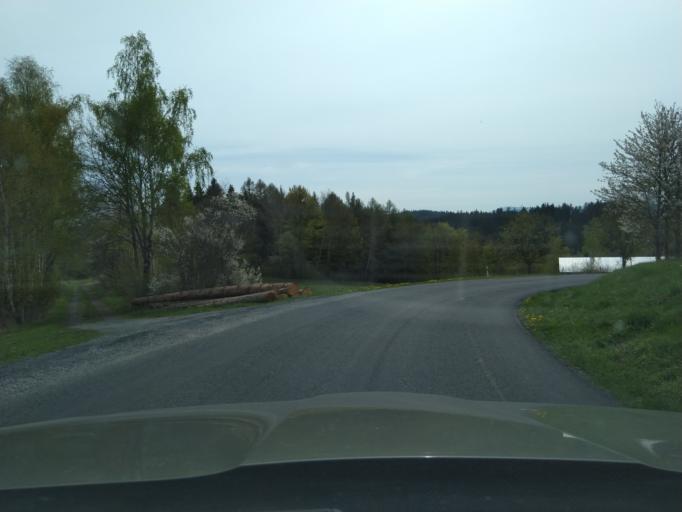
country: CZ
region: Jihocesky
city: Vacov
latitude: 49.1723
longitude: 13.6838
